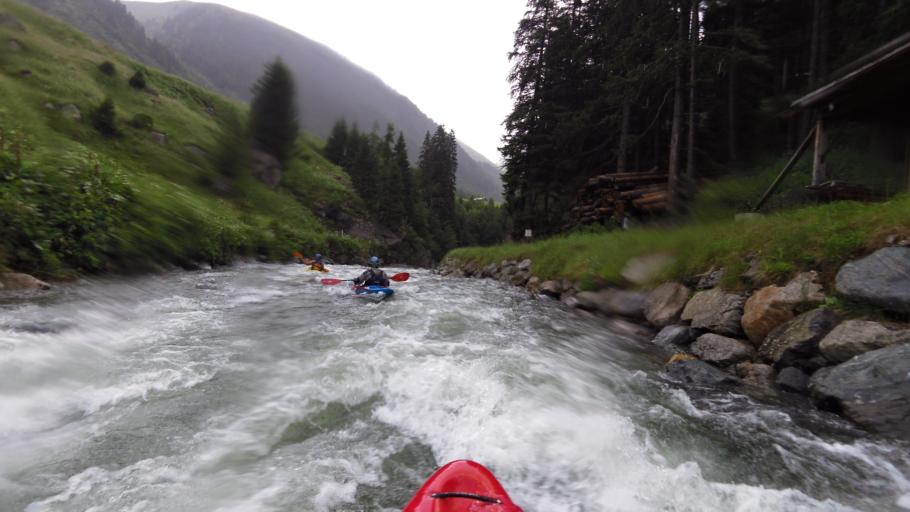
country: AT
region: Tyrol
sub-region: Politischer Bezirk Landeck
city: Galtur
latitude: 46.9781
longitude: 10.2139
